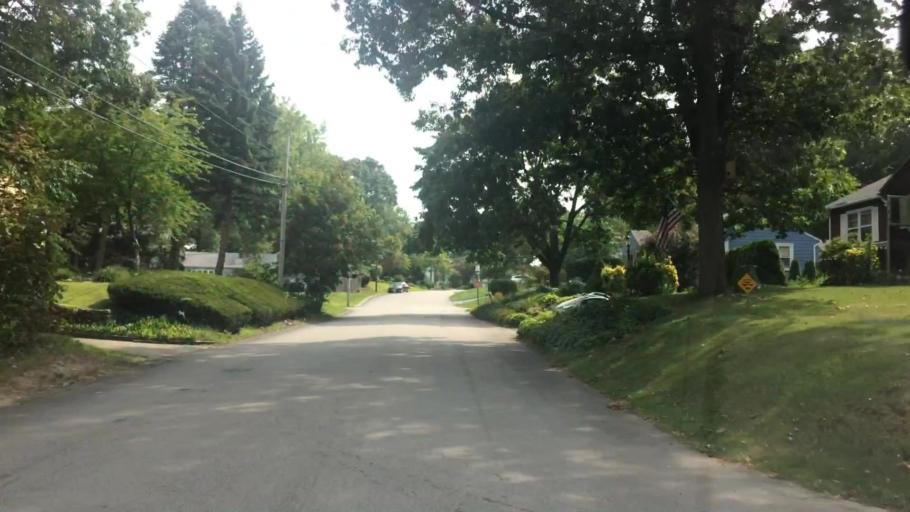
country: US
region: Rhode Island
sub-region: Kent County
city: East Greenwich
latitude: 41.7028
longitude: -71.4680
